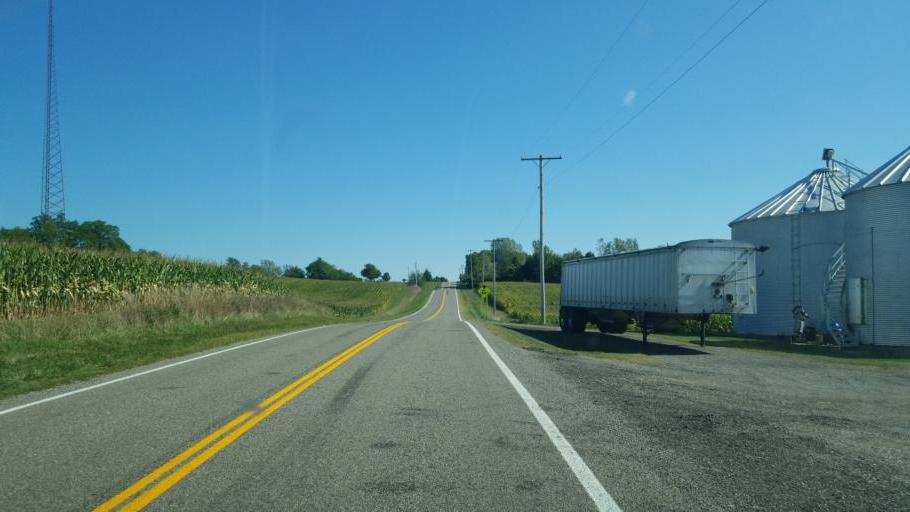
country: US
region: Ohio
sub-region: Champaign County
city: North Lewisburg
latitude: 40.1968
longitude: -83.6243
